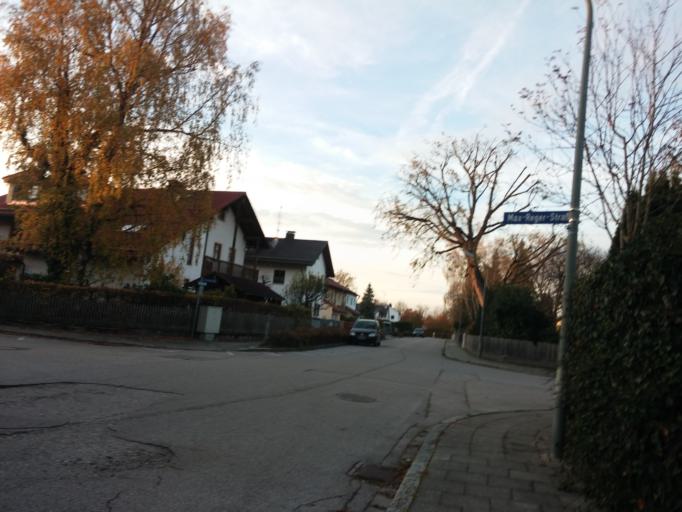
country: DE
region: Bavaria
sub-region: Upper Bavaria
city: Vaterstetten
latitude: 48.1056
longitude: 11.7782
